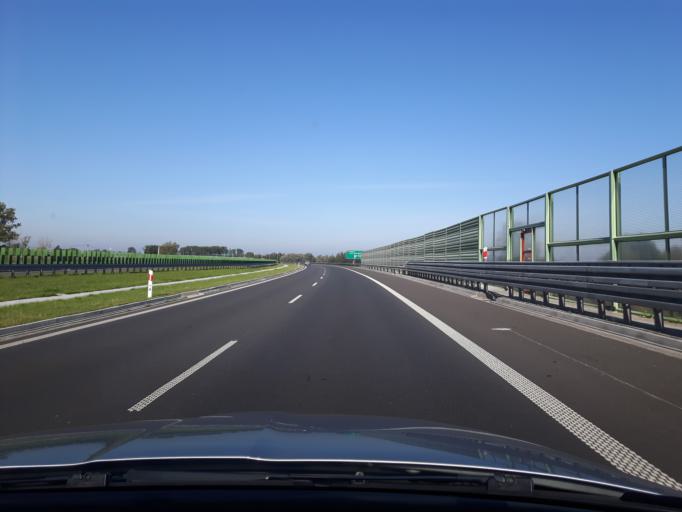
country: PL
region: Warmian-Masurian Voivodeship
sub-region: Powiat elblaski
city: Elblag
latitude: 54.1597
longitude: 19.3600
